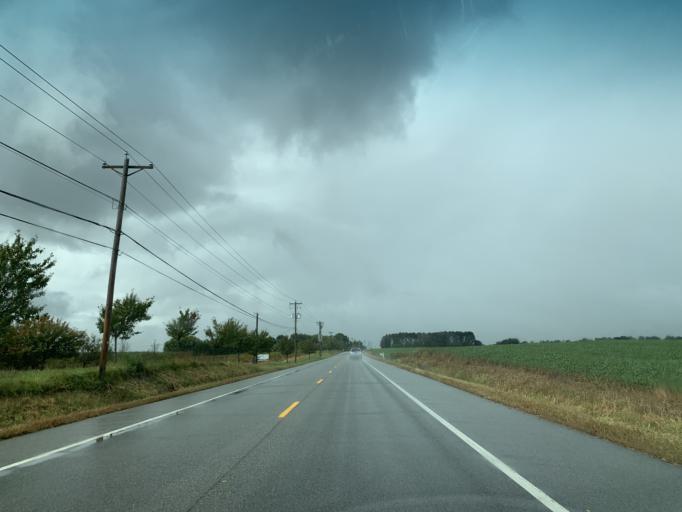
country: US
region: Maryland
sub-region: Queen Anne's County
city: Kingstown
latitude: 39.1957
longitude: -75.8614
